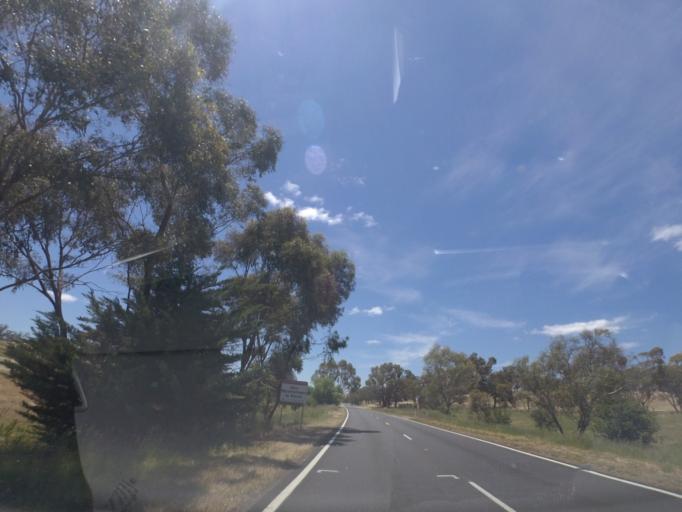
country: AU
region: Victoria
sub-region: Mount Alexander
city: Castlemaine
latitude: -37.1584
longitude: 144.1594
